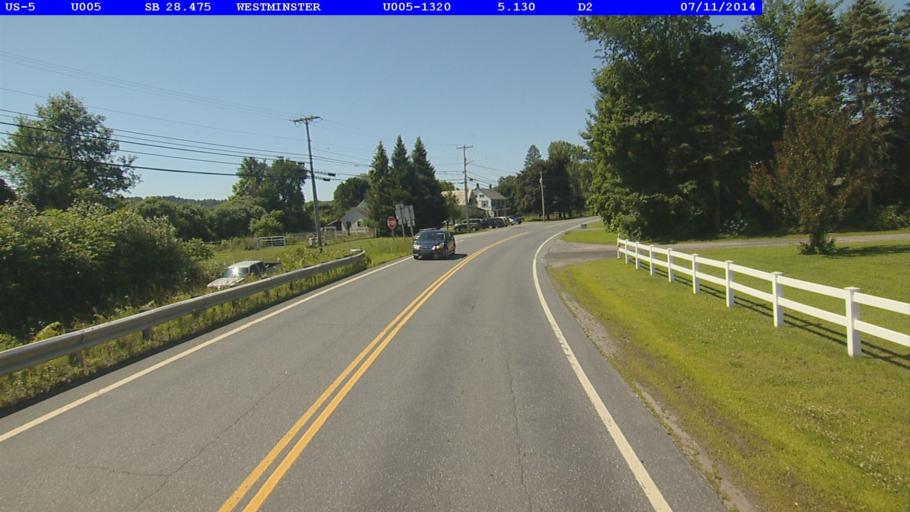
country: US
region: Vermont
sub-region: Windham County
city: Bellows Falls
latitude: 43.0853
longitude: -72.4394
